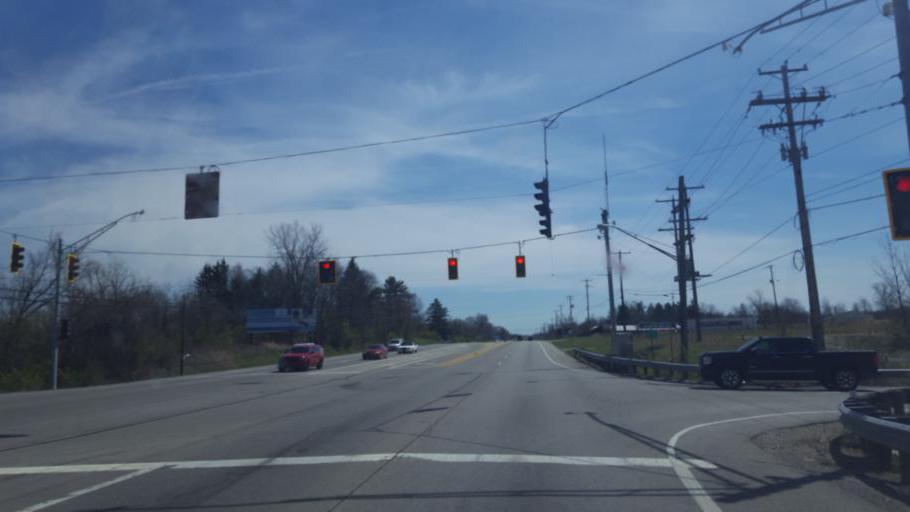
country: US
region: Ohio
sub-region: Delaware County
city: Lewis Center
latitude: 40.2138
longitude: -83.0330
